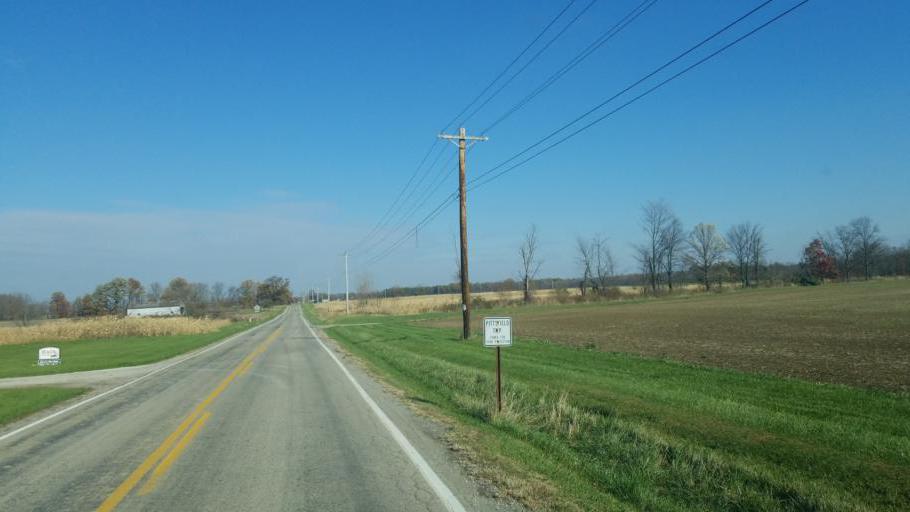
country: US
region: Ohio
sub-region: Lorain County
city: Camden
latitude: 41.2049
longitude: -82.2652
